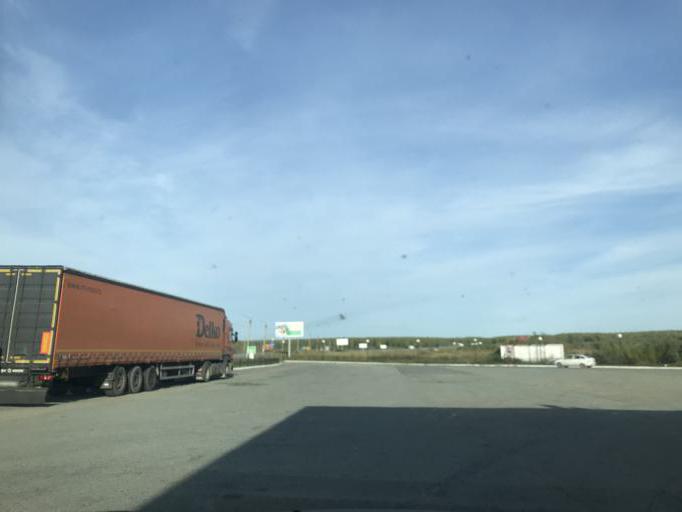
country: RU
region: Chelyabinsk
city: Poletayevo
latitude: 54.9883
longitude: 61.0441
